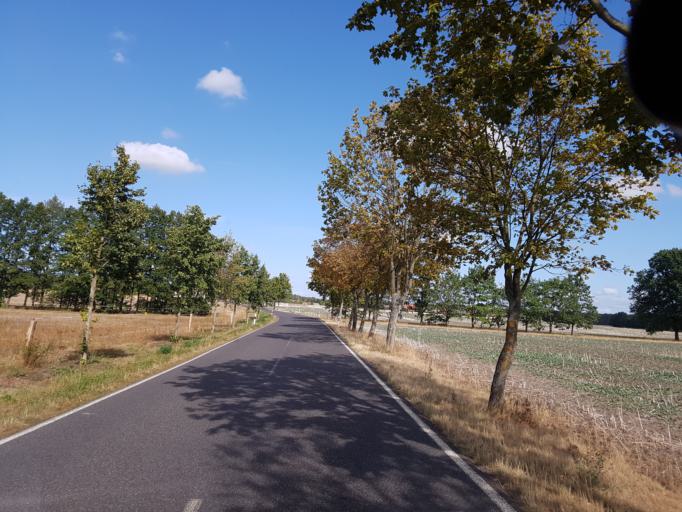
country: DE
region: Brandenburg
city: Sonnewalde
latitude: 51.7486
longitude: 13.6170
